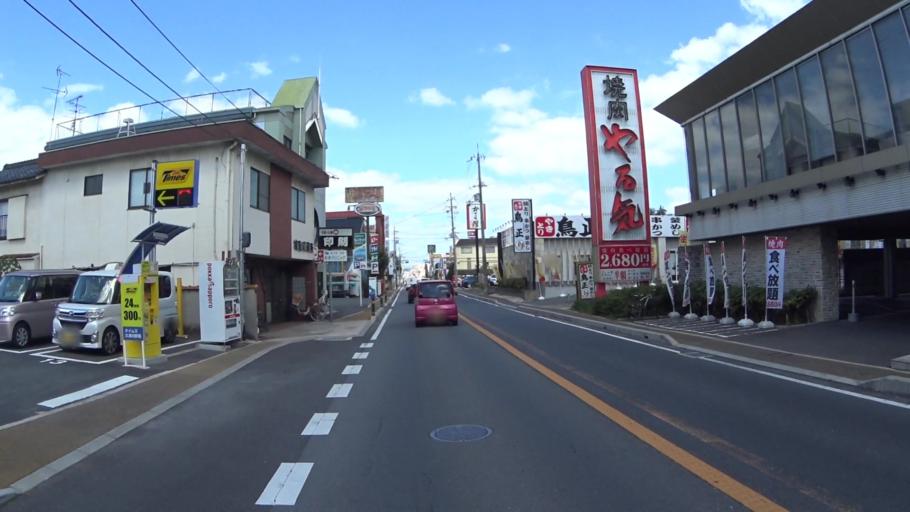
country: JP
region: Kyoto
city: Uji
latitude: 34.8652
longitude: 135.7770
